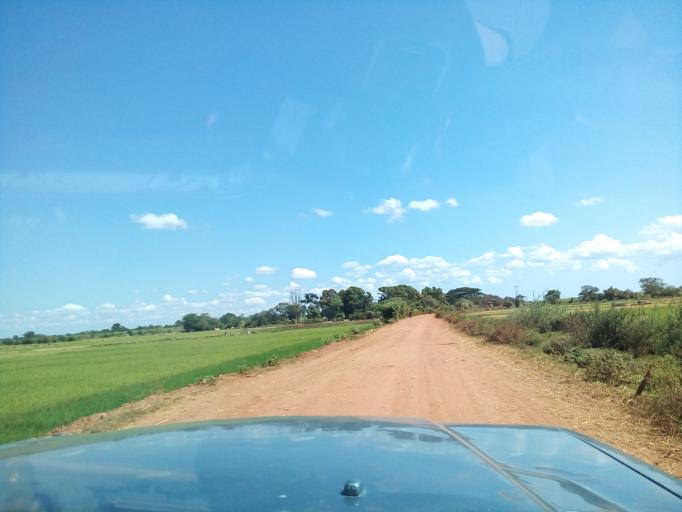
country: MG
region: Boeny
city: Mahajanga
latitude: -15.9569
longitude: 45.9335
